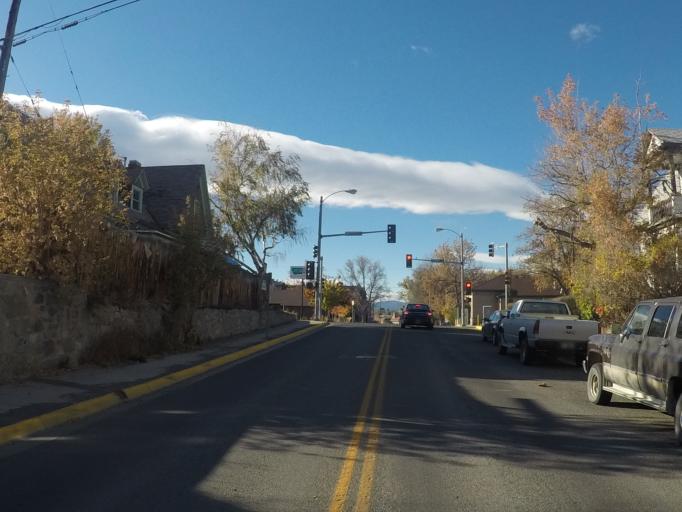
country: US
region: Montana
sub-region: Lewis and Clark County
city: Helena
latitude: 46.5868
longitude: -112.0331
